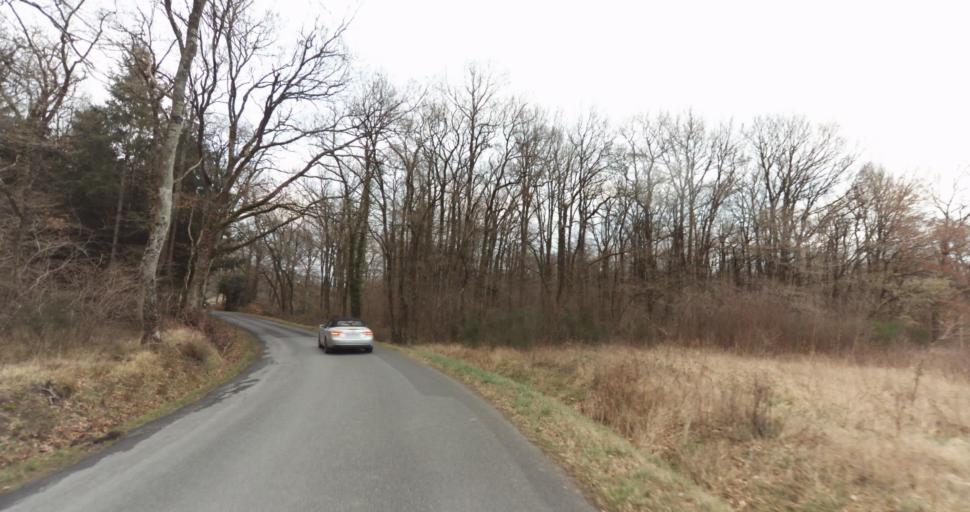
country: FR
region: Pays de la Loire
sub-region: Departement de Maine-et-Loire
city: Distre
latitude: 47.2552
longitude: -0.1268
